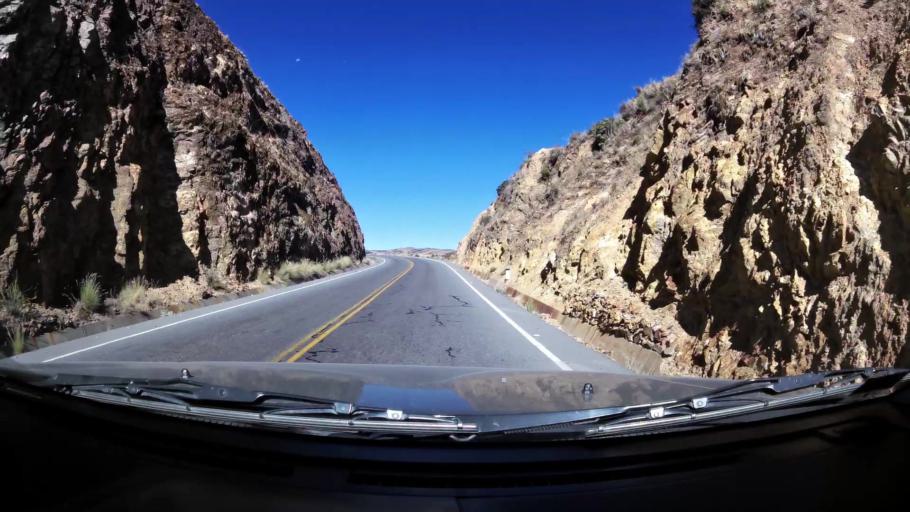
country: PE
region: Huancavelica
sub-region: Huaytara
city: Huayacundo Arma
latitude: -13.5624
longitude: -75.2418
